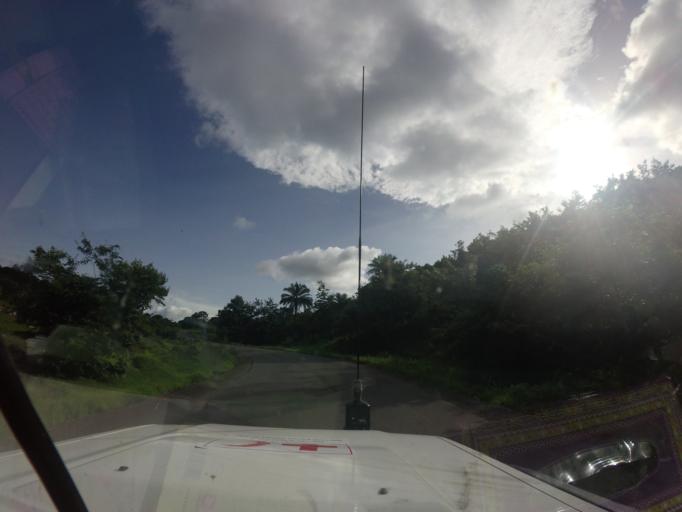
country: GN
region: Kindia
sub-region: Kindia
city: Kindia
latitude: 10.1442
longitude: -12.5419
